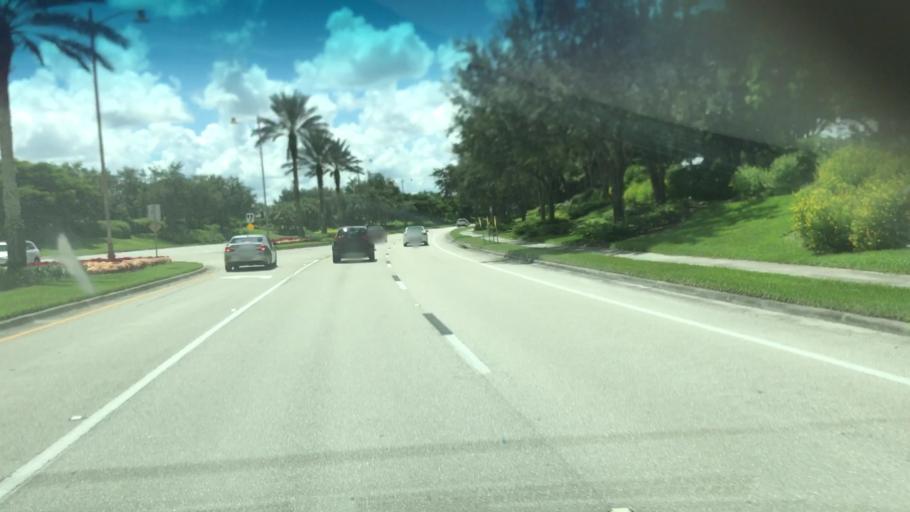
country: US
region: Florida
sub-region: Lee County
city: Estero
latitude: 26.4093
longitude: -81.7826
